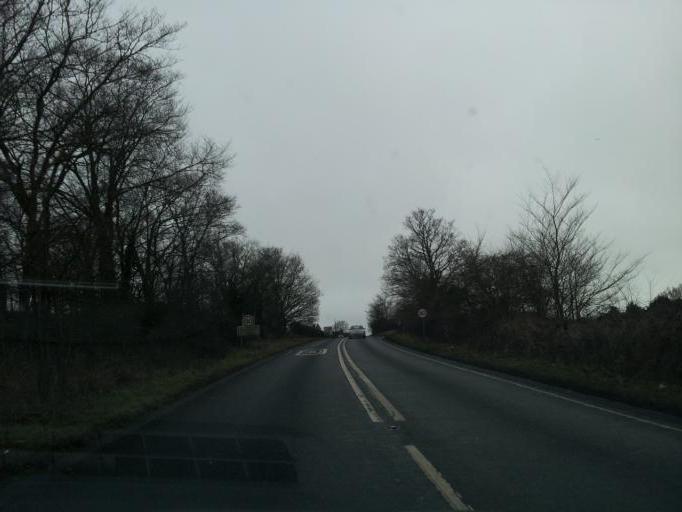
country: GB
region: England
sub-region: Essex
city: Mistley
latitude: 51.9710
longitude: 1.0900
